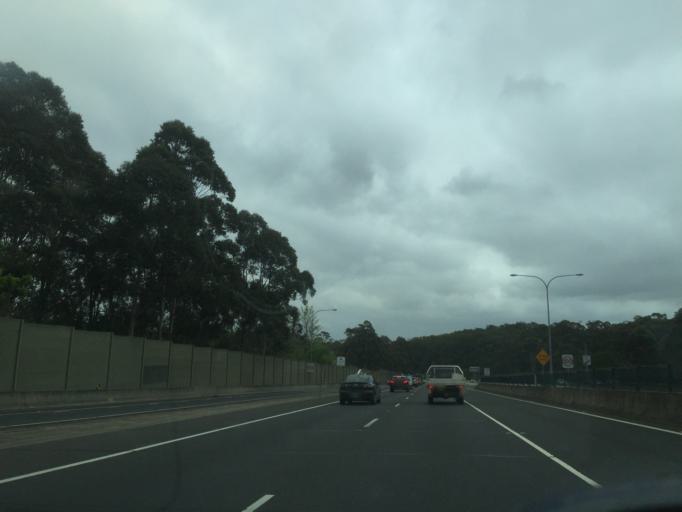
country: AU
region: New South Wales
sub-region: The Hills Shire
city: West Pennant
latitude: -33.7600
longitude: 151.0409
